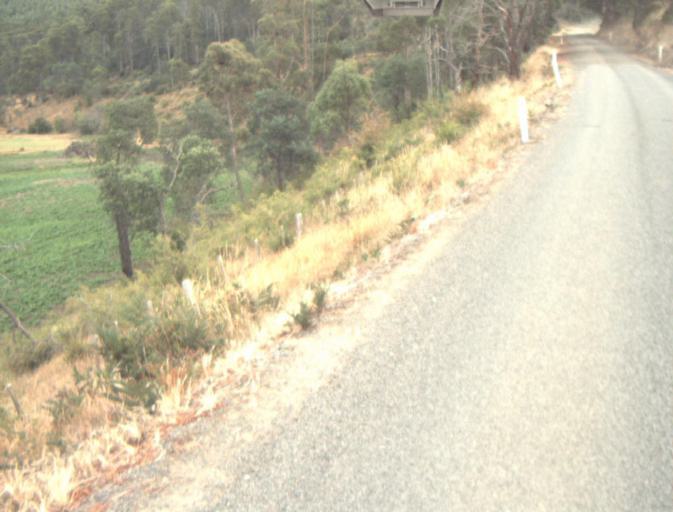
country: AU
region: Tasmania
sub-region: Northern Midlands
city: Evandale
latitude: -41.4741
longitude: 147.5346
